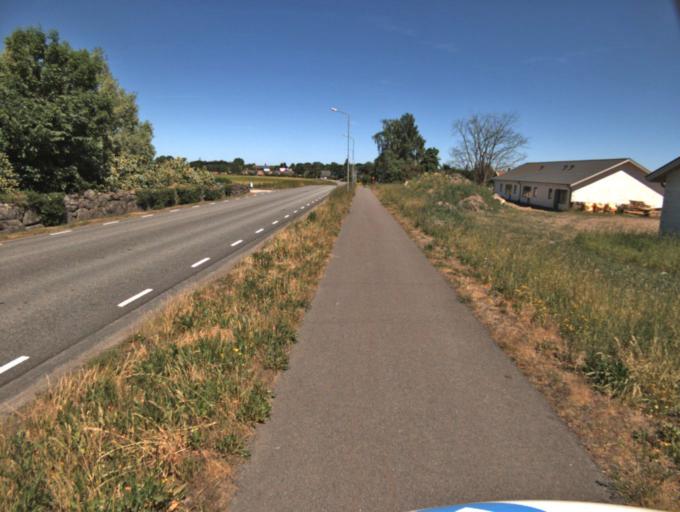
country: SE
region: Skane
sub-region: Kristianstads Kommun
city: Onnestad
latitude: 56.0529
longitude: 14.0142
